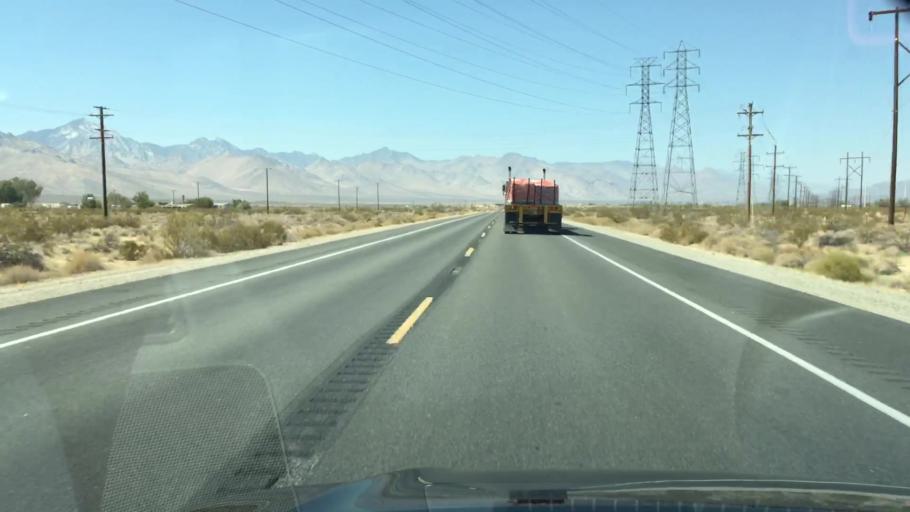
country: US
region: California
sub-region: Kern County
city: Inyokern
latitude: 35.6410
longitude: -117.7916
